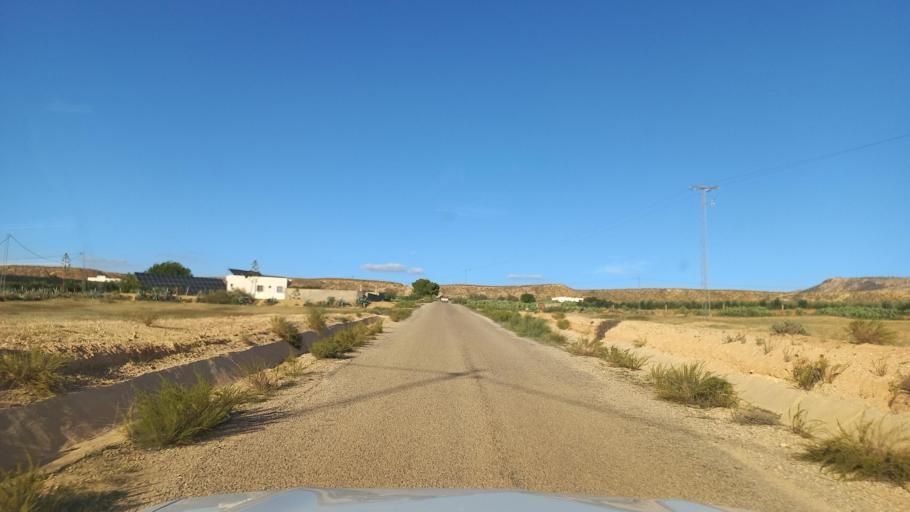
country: TN
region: Al Qasrayn
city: Sbiba
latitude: 35.3444
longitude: 9.1264
